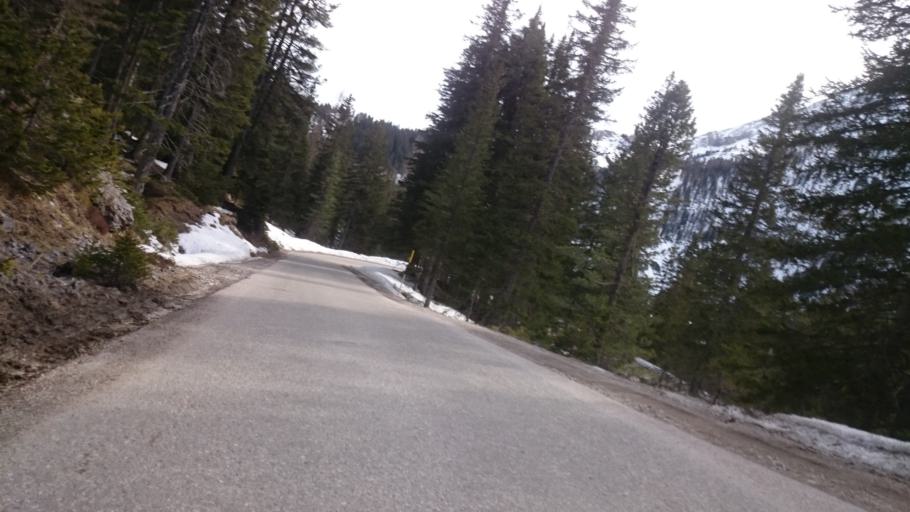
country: IT
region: Trentino-Alto Adige
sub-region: Bolzano
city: Braies
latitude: 46.6603
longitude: 12.1678
